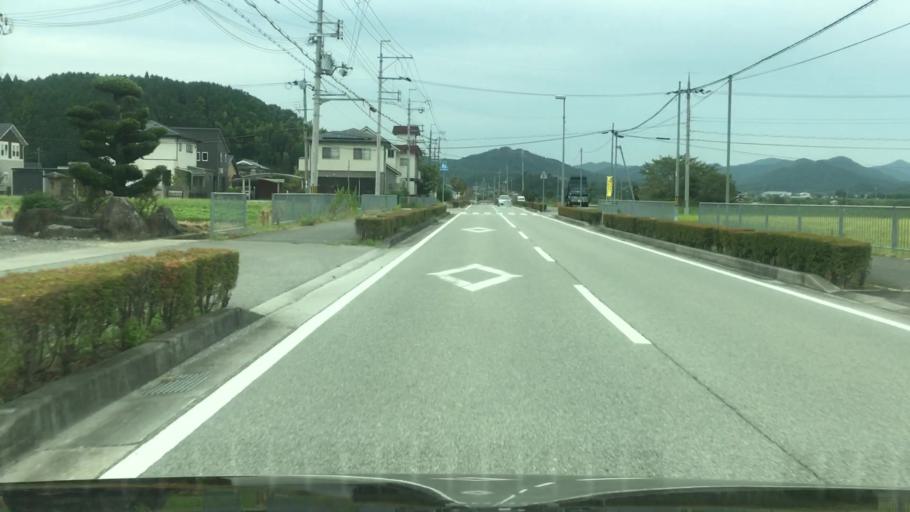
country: JP
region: Hyogo
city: Sasayama
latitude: 35.0724
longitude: 135.1872
